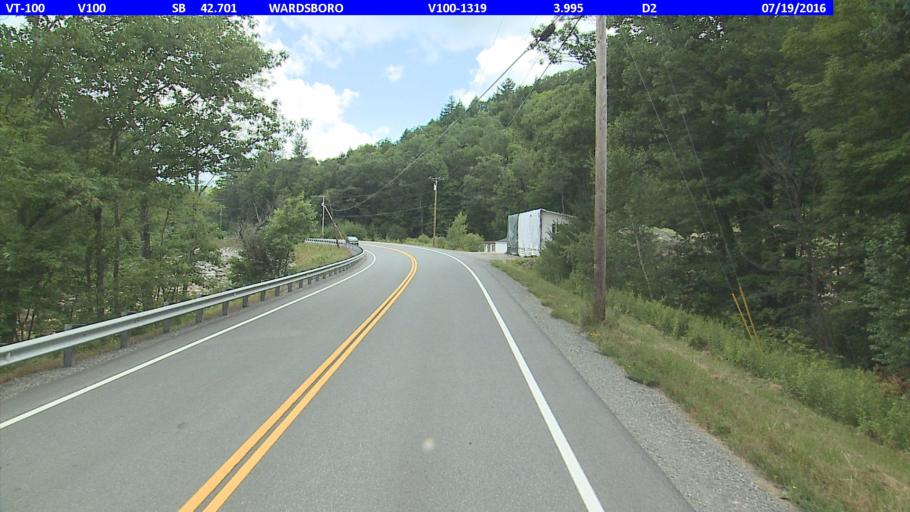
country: US
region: Vermont
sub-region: Windham County
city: Dover
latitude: 43.0555
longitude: -72.8594
